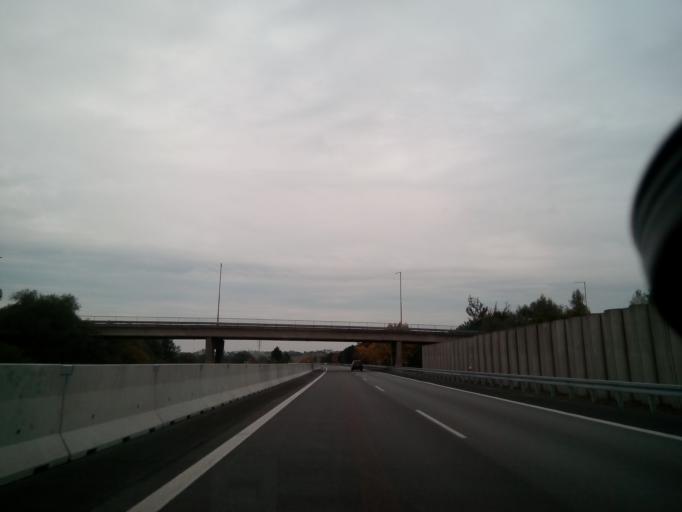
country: SK
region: Presovsky
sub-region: Okres Presov
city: Presov
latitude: 48.9244
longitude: 21.2568
